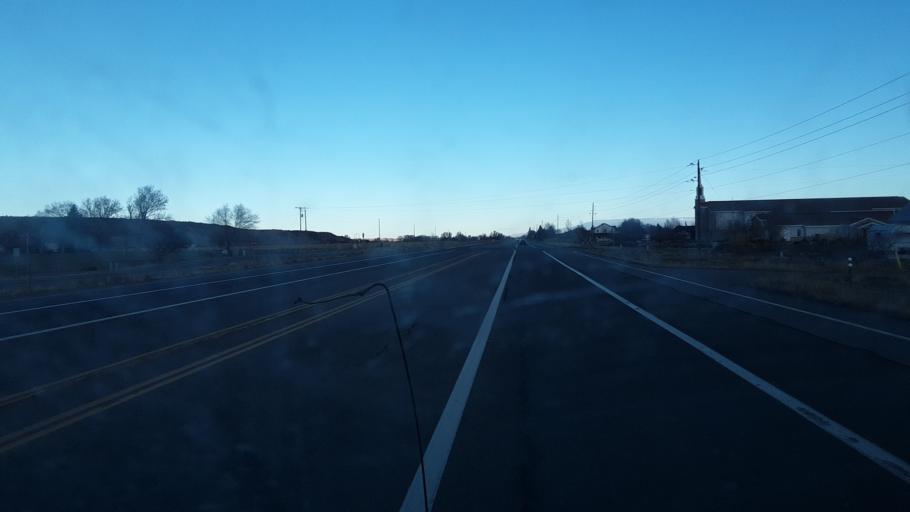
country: US
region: Colorado
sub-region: Montrose County
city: Montrose
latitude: 38.3771
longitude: -107.8178
